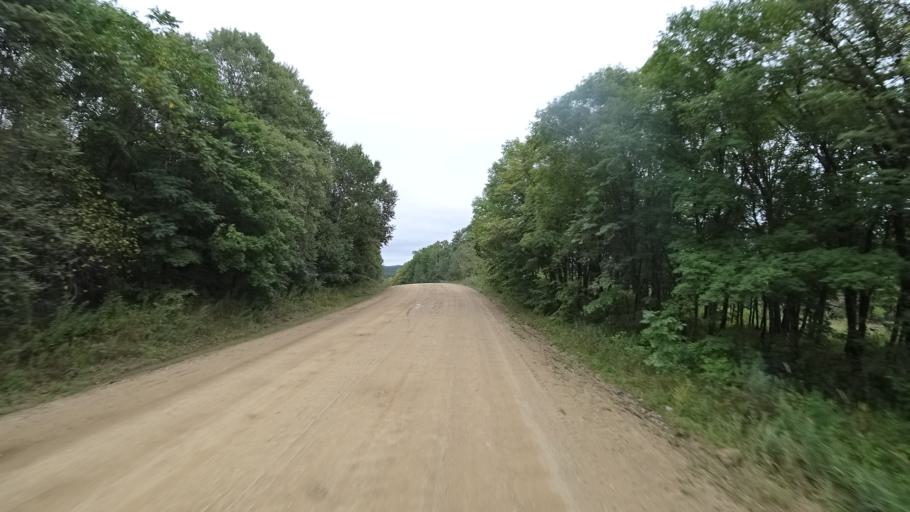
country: RU
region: Primorskiy
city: Rettikhovka
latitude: 44.1753
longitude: 132.8321
